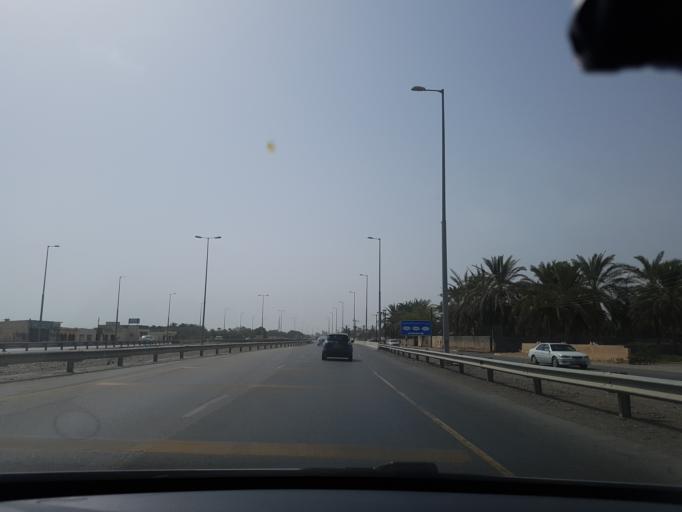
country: OM
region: Al Batinah
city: Al Khaburah
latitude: 23.9831
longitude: 57.0799
